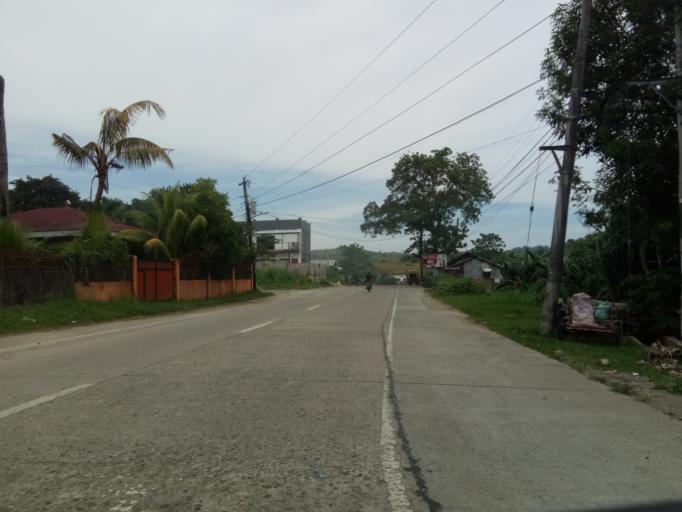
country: PH
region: Caraga
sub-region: Province of Surigao del Norte
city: Surigao
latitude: 9.7739
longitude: 125.4911
